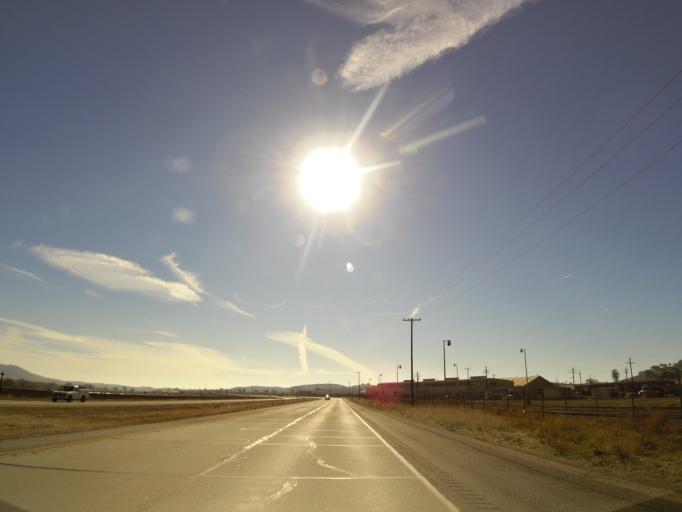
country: US
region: California
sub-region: San Luis Obispo County
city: San Miguel
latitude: 35.7854
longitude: -120.7272
